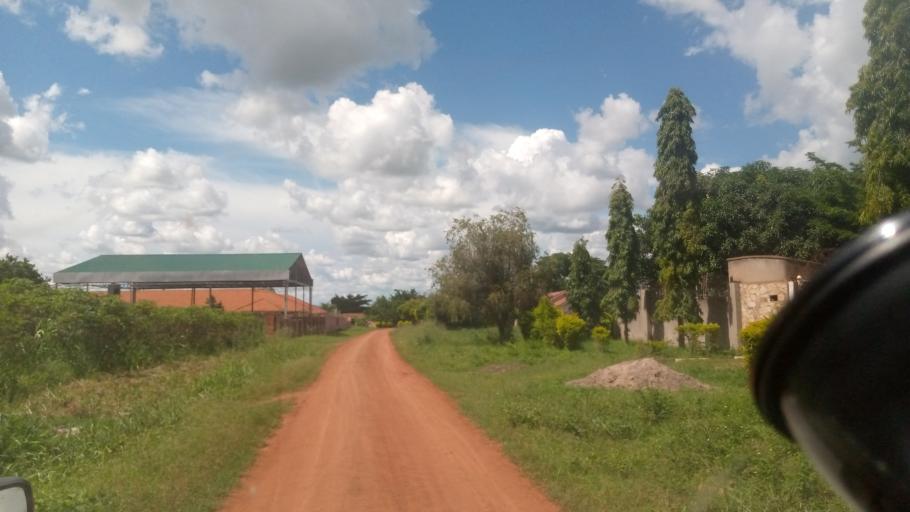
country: UG
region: Northern Region
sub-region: Lira District
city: Lira
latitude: 2.2365
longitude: 32.9049
